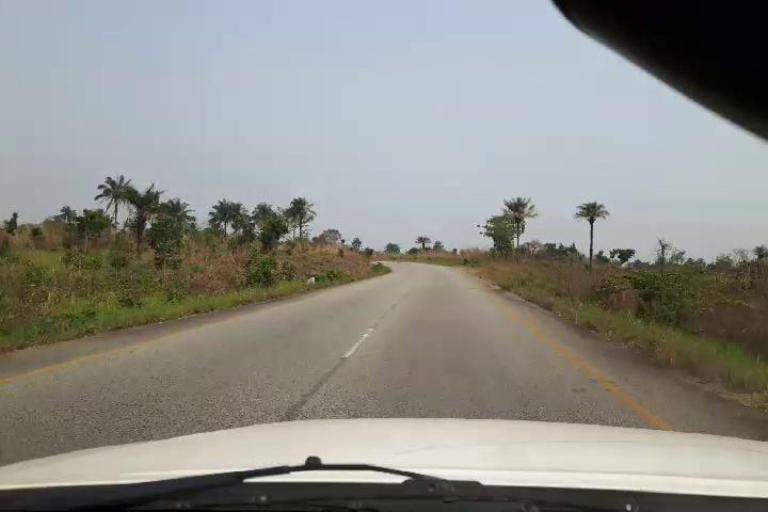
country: SL
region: Southern Province
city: Largo
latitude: 8.3036
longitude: -12.2016
